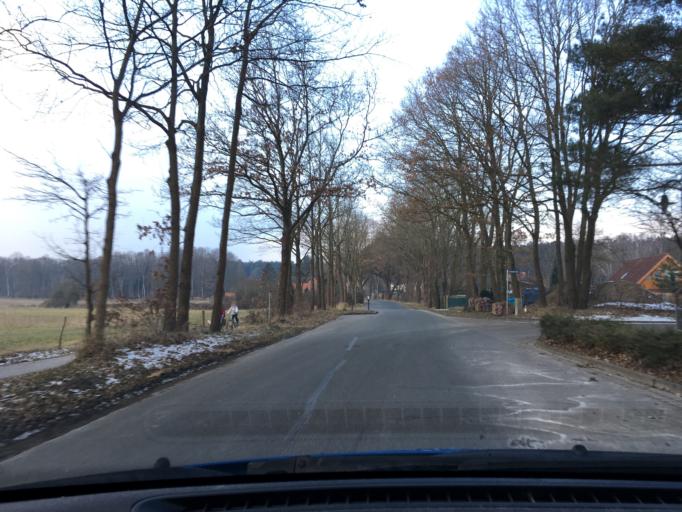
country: DE
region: Lower Saxony
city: Bienenbuttel
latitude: 53.1486
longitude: 10.4897
